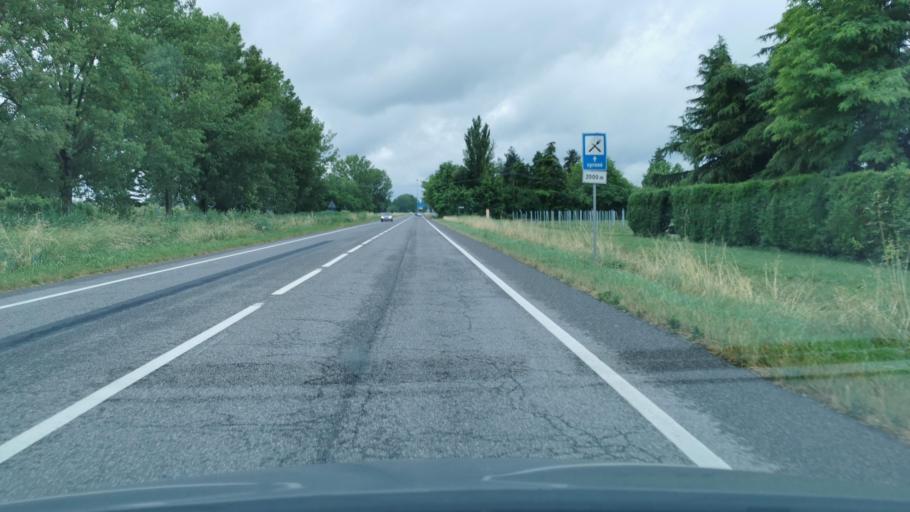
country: IT
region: Emilia-Romagna
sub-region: Provincia di Ravenna
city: Cotignola
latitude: 44.3886
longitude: 11.9549
